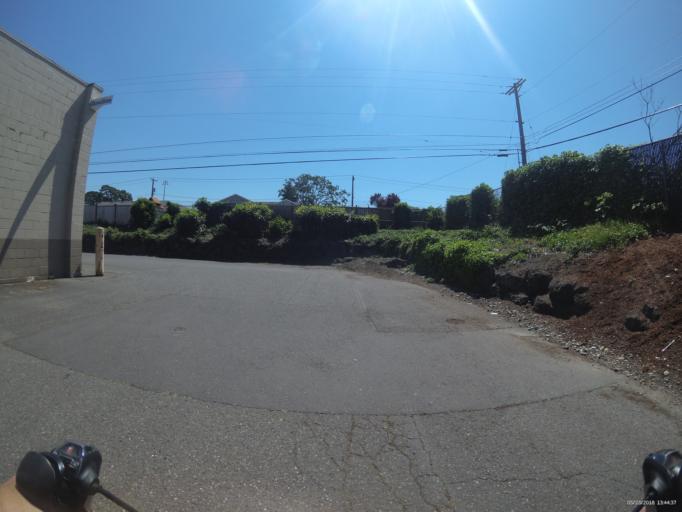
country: US
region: Washington
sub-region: Pierce County
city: Lakewood
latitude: 47.1617
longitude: -122.5189
